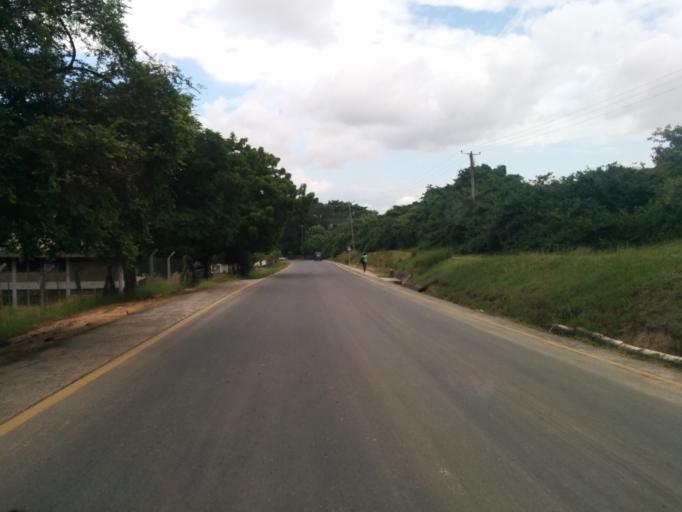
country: TZ
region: Dar es Salaam
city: Magomeni
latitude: -6.7833
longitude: 39.2062
